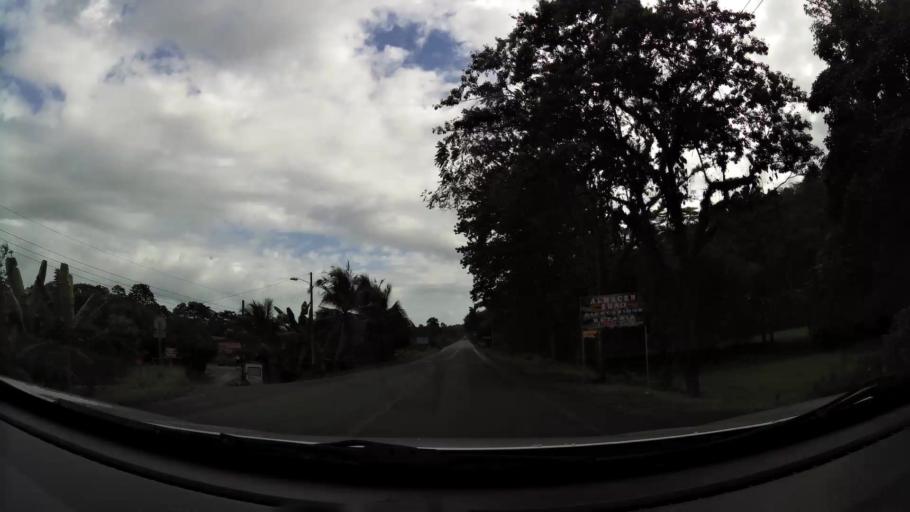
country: CR
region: Limon
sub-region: Canton de Siquirres
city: Siquirres
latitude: 10.0918
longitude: -83.4890
